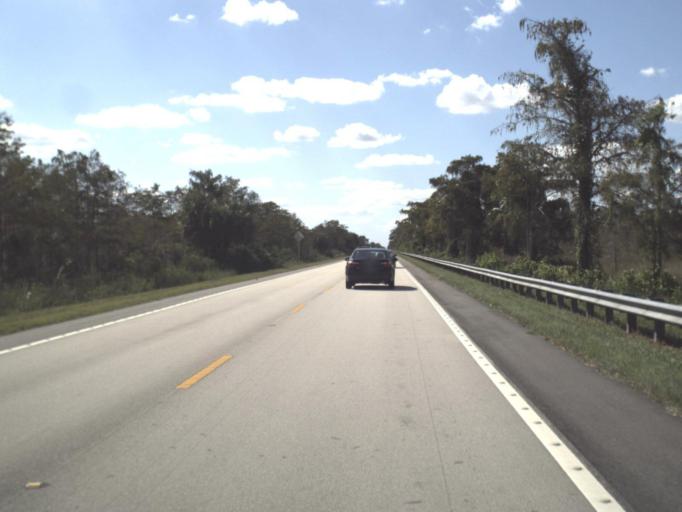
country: US
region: Florida
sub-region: Collier County
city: Lely Resort
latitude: 25.8629
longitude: -81.0925
